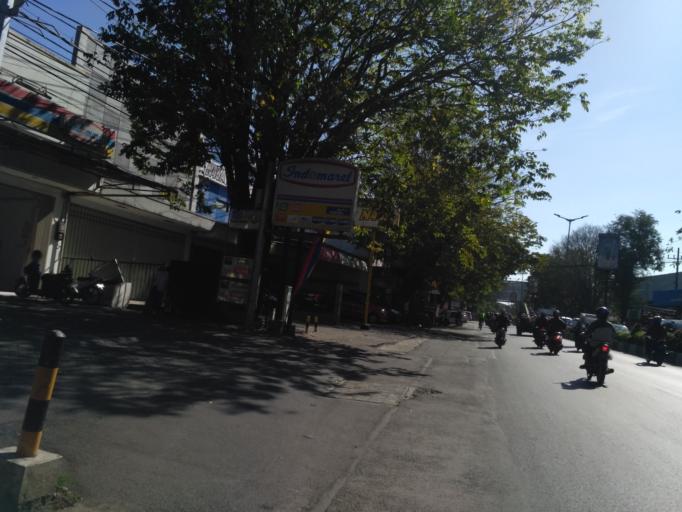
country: ID
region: East Java
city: Malang
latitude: -7.9391
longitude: 112.6434
